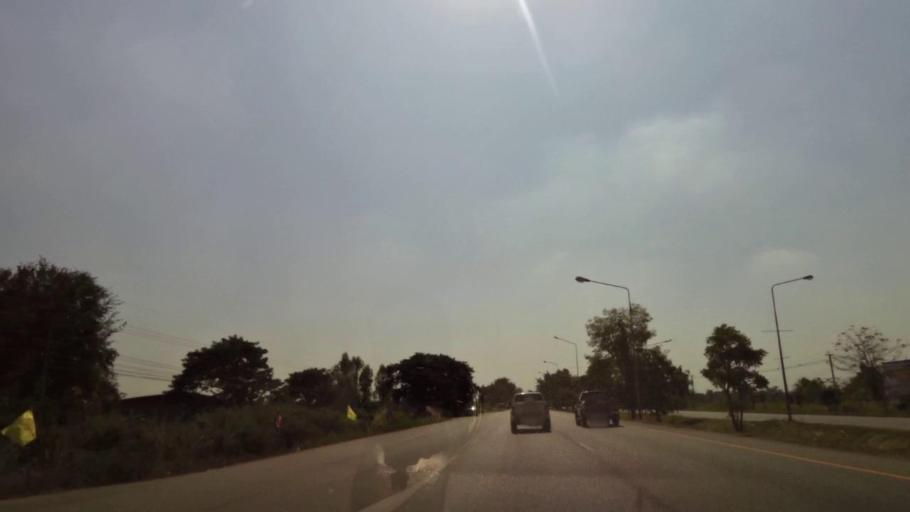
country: TH
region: Phichit
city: Wachira Barami
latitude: 16.4102
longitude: 100.1429
